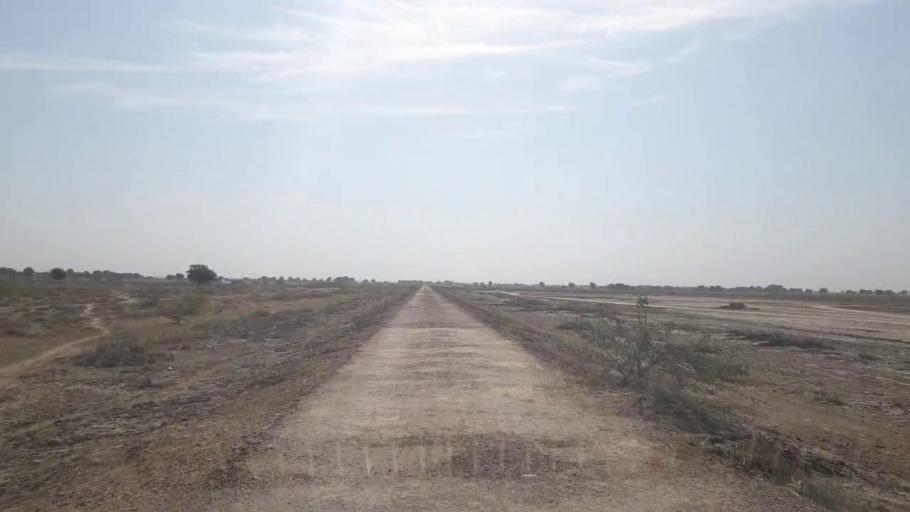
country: PK
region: Sindh
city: Umarkot
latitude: 25.2851
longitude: 69.6556
